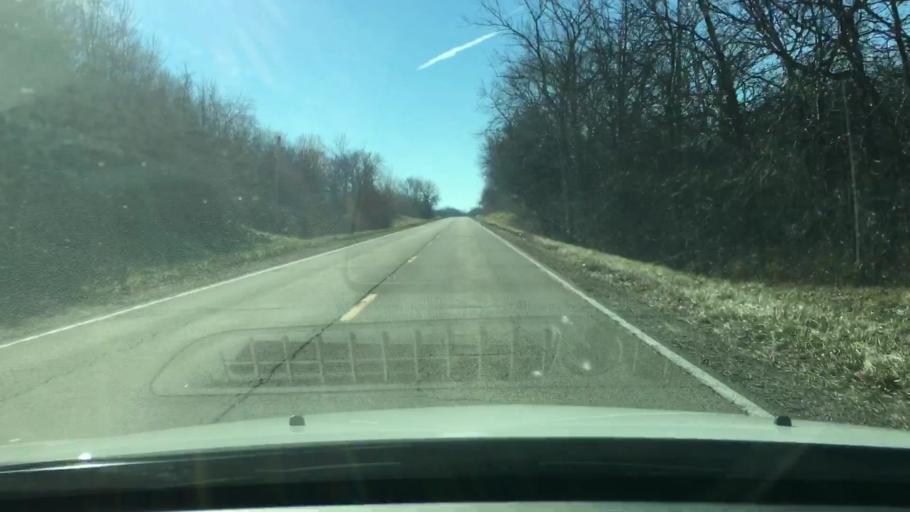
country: US
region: Illinois
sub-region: Mason County
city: Havana
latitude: 40.2963
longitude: -90.1518
